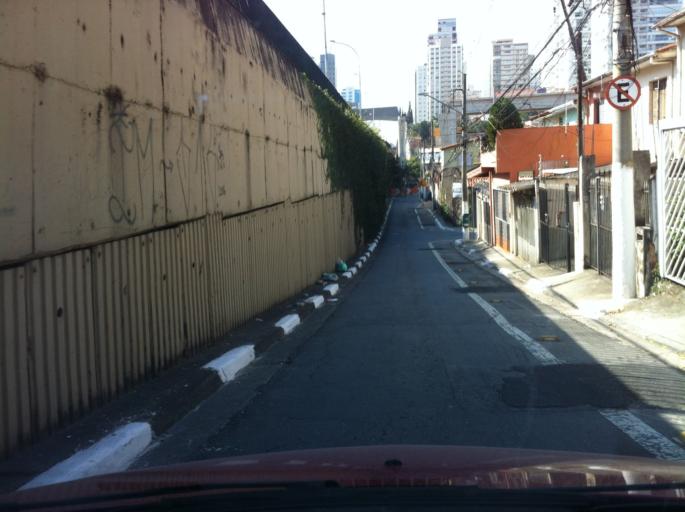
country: BR
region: Sao Paulo
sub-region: Diadema
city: Diadema
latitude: -23.6229
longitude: -46.6801
